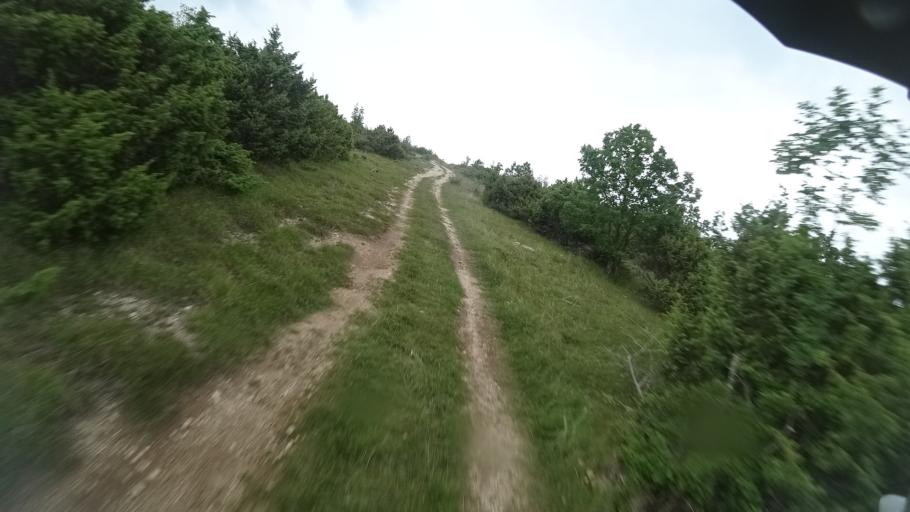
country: HR
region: Sibensko-Kniniska
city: Knin
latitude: 44.0317
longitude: 16.2545
